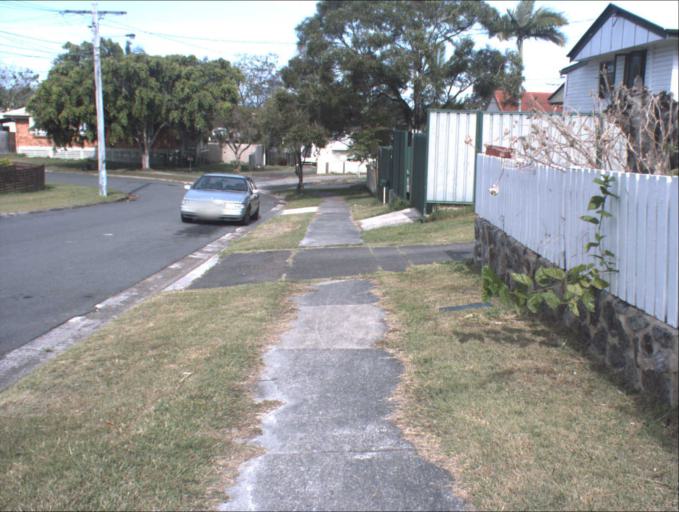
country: AU
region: Queensland
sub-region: Logan
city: Woodridge
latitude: -27.6334
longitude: 153.0993
